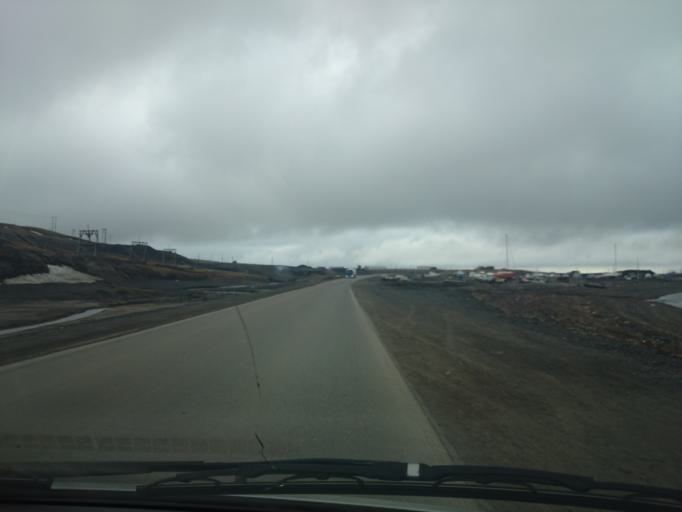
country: SJ
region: Svalbard
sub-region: Spitsbergen
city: Longyearbyen
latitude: 78.2355
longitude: 15.5511
